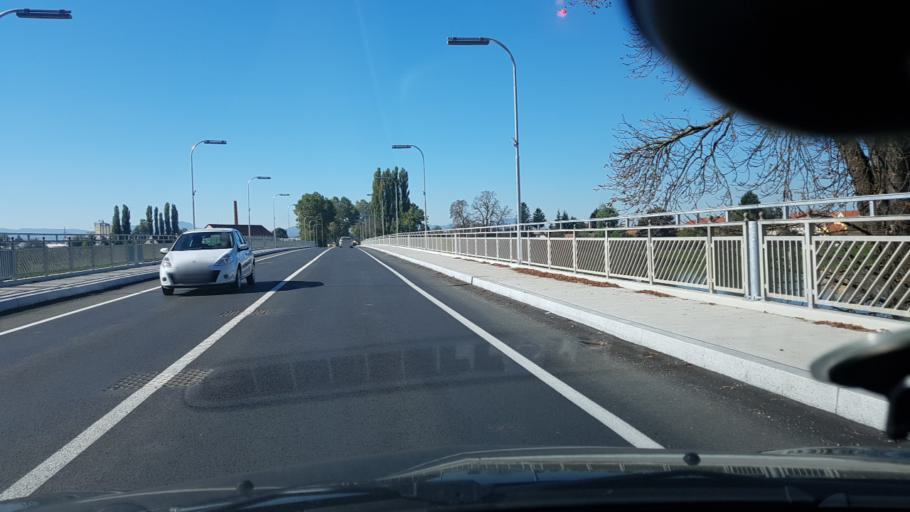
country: SI
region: Ptuj
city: Ptuj
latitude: 46.4174
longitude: 15.8703
